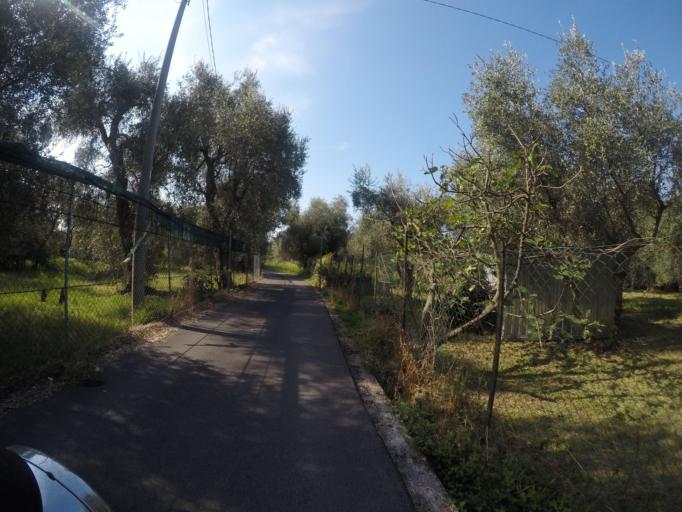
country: IT
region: Tuscany
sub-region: Provincia di Massa-Carrara
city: Massa
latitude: 44.0297
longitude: 10.1216
